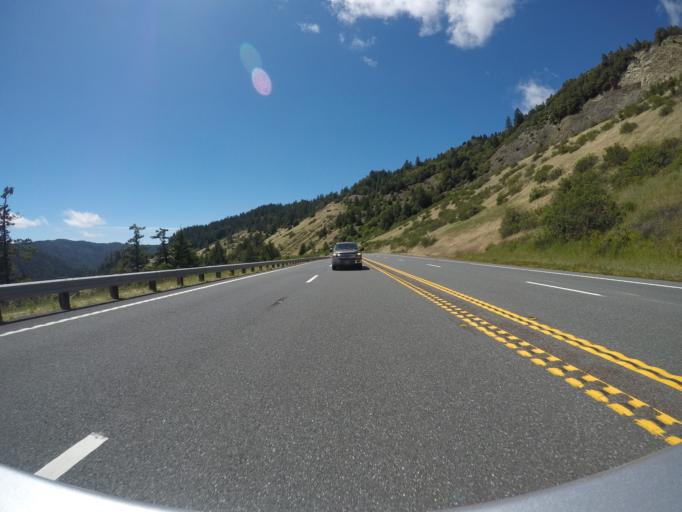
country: US
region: California
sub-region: Mendocino County
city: Laytonville
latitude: 39.8287
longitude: -123.6572
